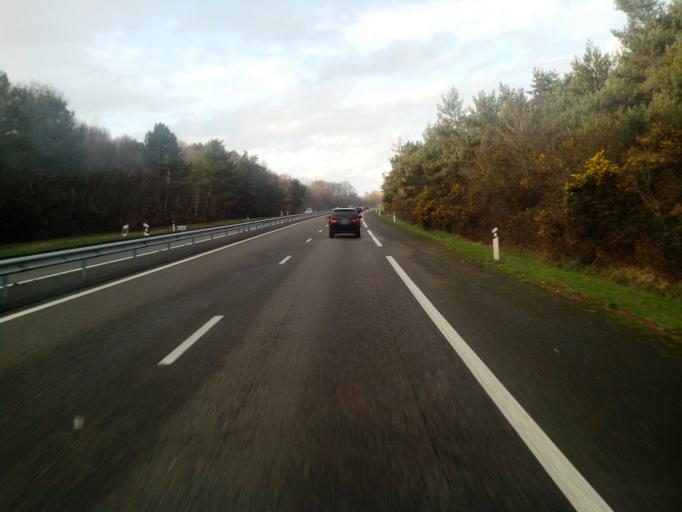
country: FR
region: Brittany
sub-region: Departement d'Ille-et-Vilaine
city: Saint-Pierre-de-Plesguen
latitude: 48.4324
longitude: -1.9178
